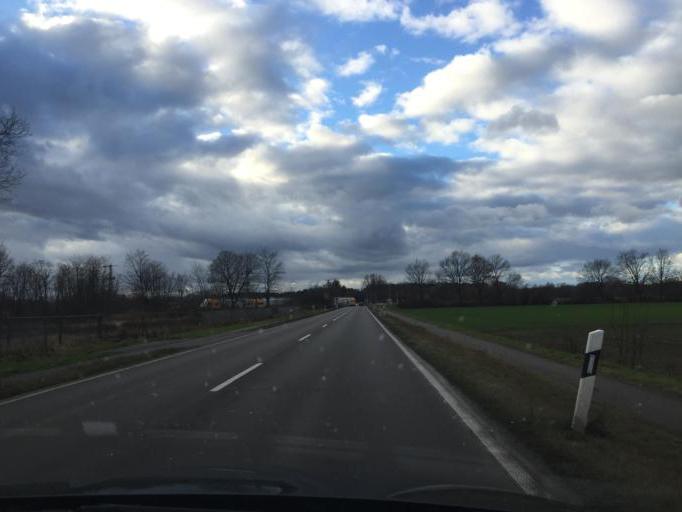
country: DE
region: Brandenburg
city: Kolkwitz
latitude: 51.7523
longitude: 14.2877
